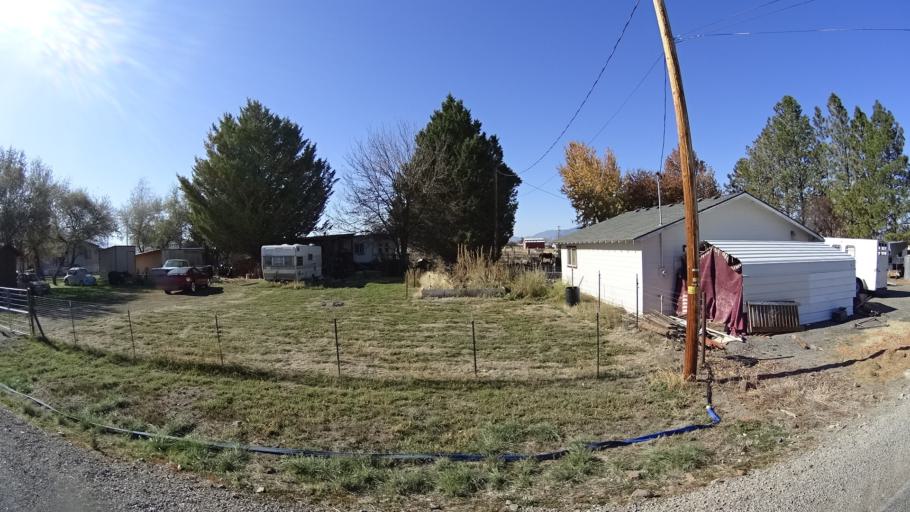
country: US
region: California
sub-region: Siskiyou County
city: Montague
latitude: 41.7545
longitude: -122.4572
